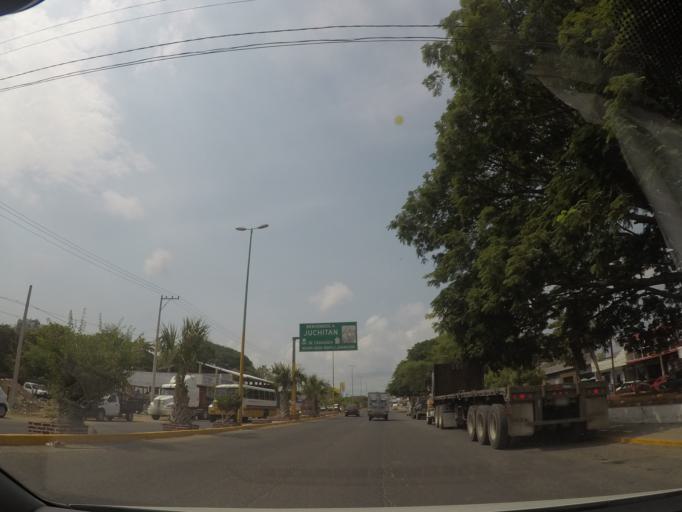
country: MX
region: Oaxaca
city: Juchitan de Zaragoza
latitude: 16.4494
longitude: -95.0263
